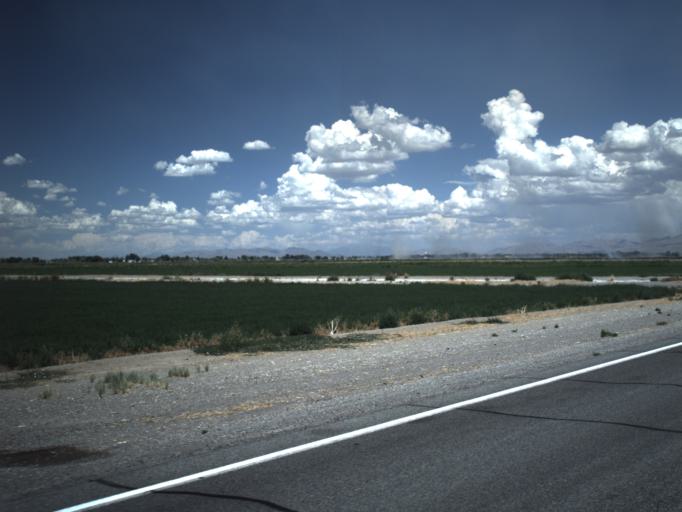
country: US
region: Utah
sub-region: Millard County
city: Delta
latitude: 39.3306
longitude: -112.6391
